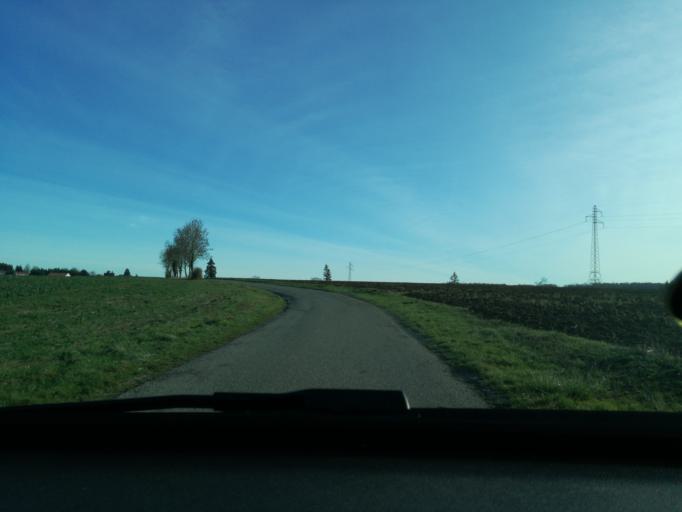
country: FR
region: Lorraine
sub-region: Departement de la Meuse
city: Fains-Veel
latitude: 48.8151
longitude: 5.0705
